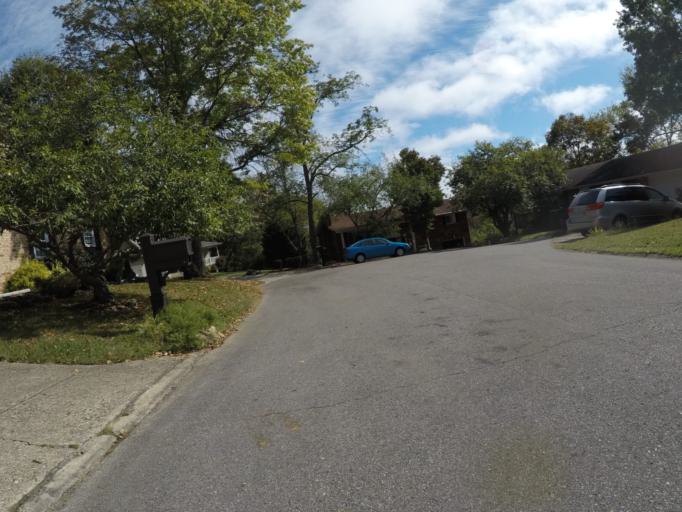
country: US
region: West Virginia
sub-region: Cabell County
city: Huntington
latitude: 38.3952
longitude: -82.3929
